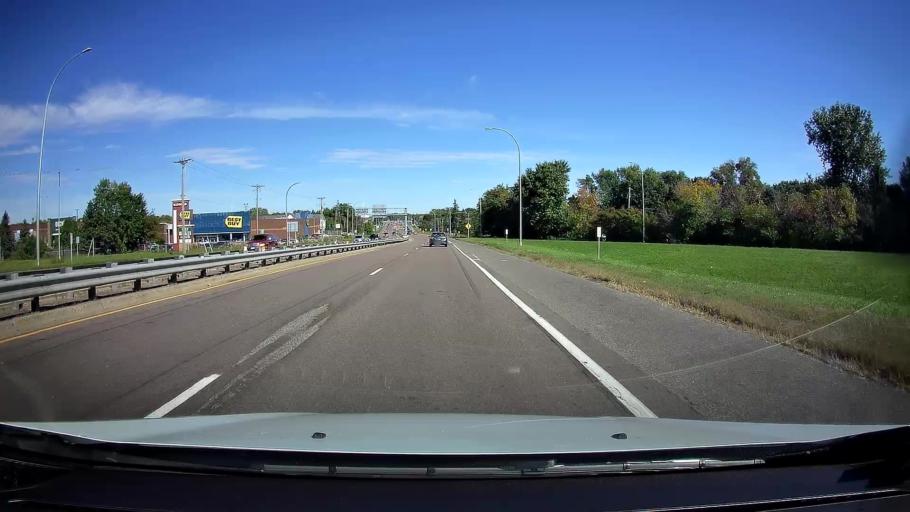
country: US
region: Minnesota
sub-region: Ramsey County
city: Roseville
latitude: 45.0144
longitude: -93.1669
